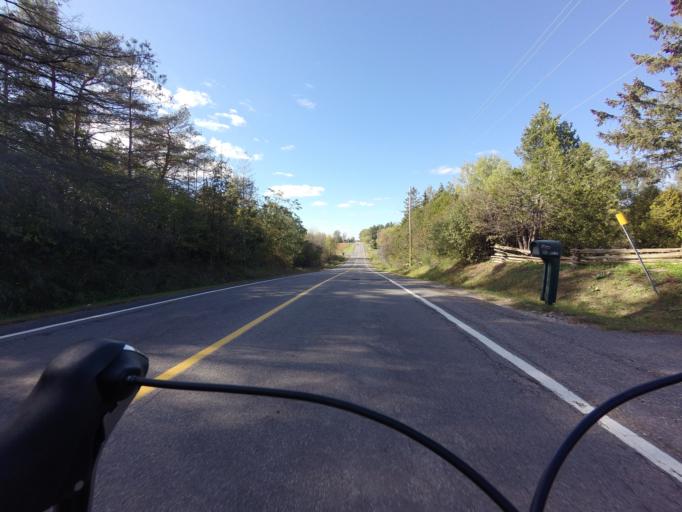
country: CA
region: Ontario
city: Bells Corners
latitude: 45.1103
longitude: -75.7240
